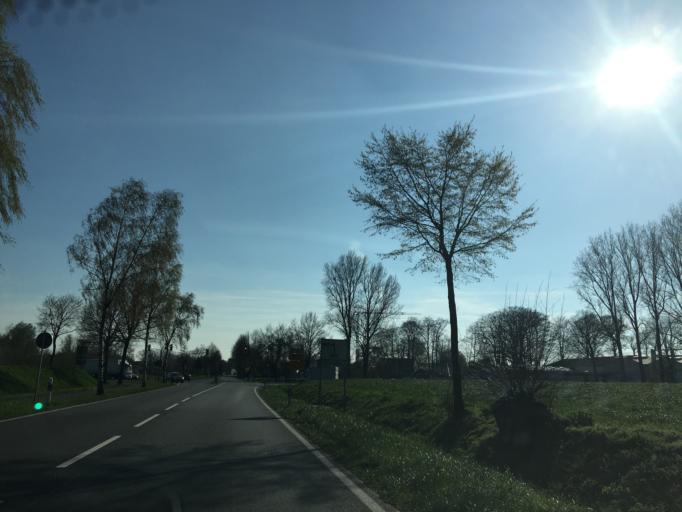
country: DE
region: North Rhine-Westphalia
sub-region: Regierungsbezirk Munster
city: Greven
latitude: 52.1066
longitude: 7.6276
